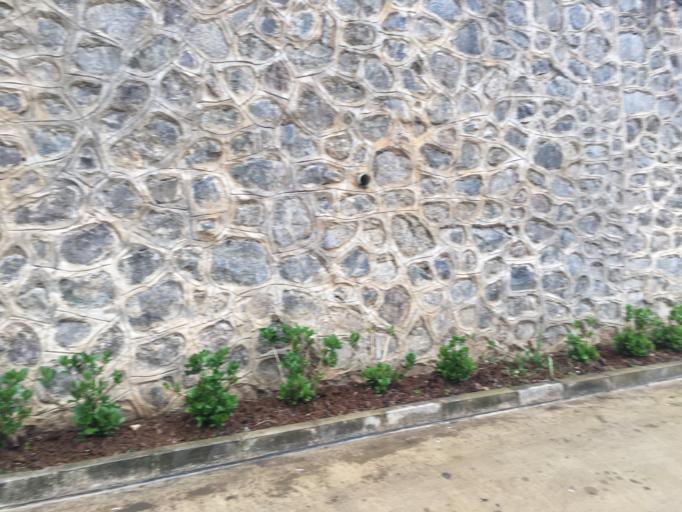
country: TR
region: Trabzon
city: Trabzon
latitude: 40.9920
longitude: 39.7763
